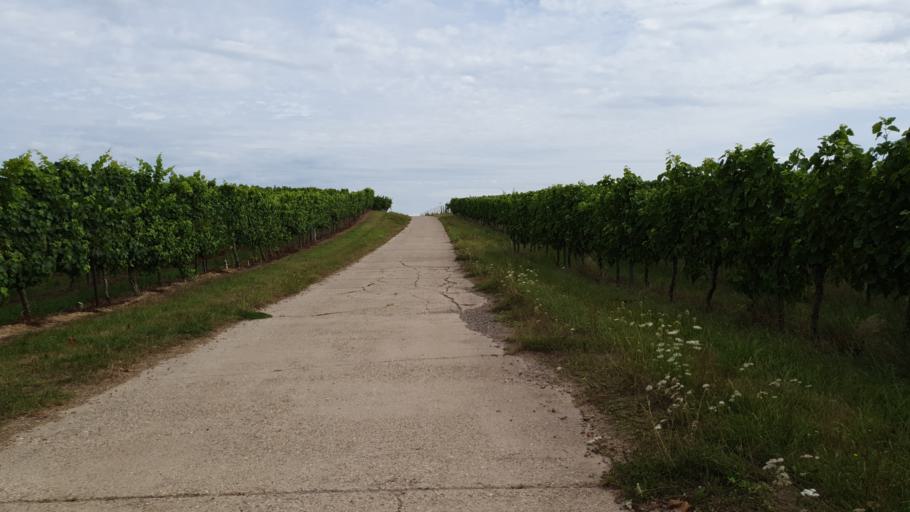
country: DE
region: Rheinland-Pfalz
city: Billigheim-Ingenheim
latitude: 49.1192
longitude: 8.0826
